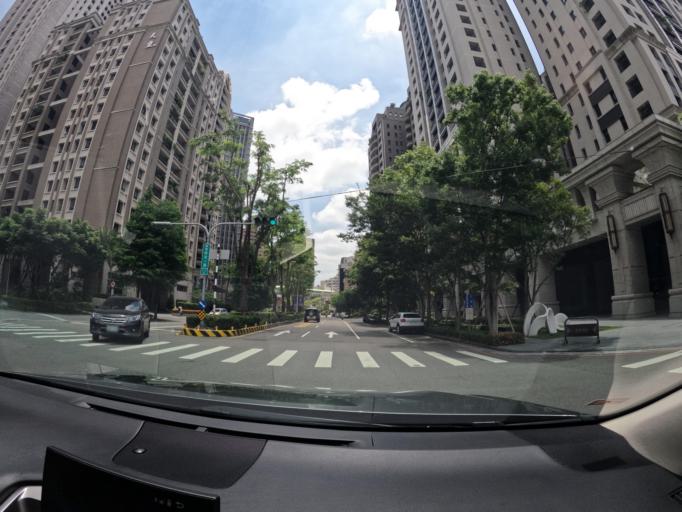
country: TW
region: Taiwan
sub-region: Taichung City
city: Taichung
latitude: 24.1577
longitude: 120.6447
